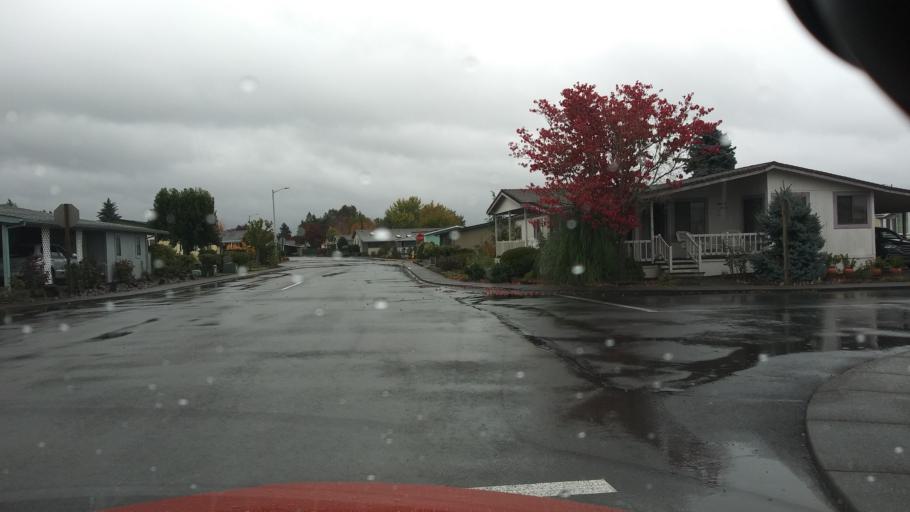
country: US
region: Oregon
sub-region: Washington County
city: Cornelius
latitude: 45.5131
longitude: -123.0734
